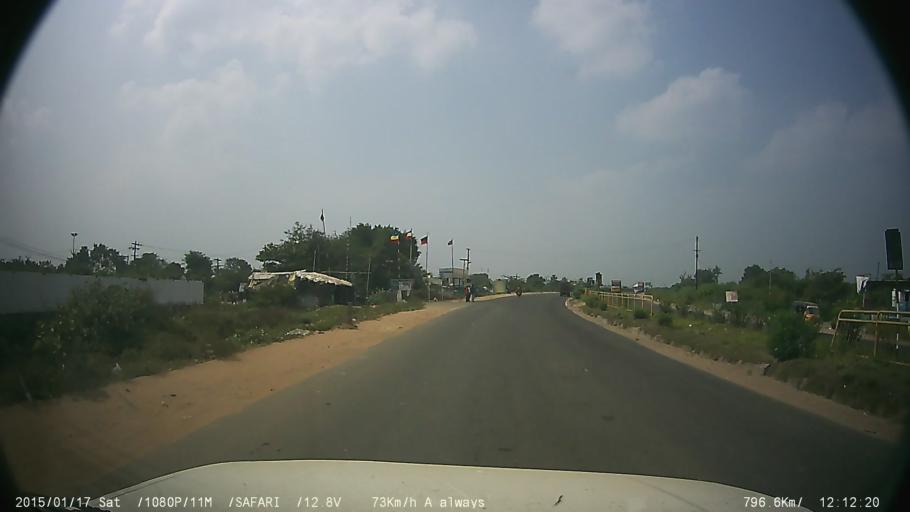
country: IN
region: Tamil Nadu
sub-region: Kancheepuram
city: Sriperumbudur
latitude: 12.9332
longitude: 79.9053
